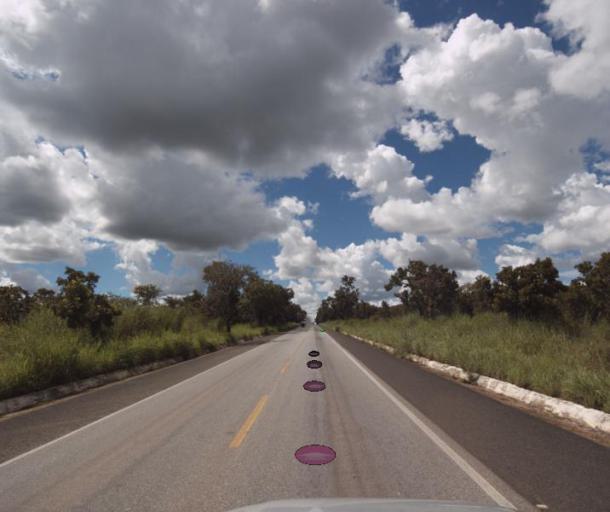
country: BR
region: Goias
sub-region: Porangatu
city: Porangatu
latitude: -13.7993
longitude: -49.0366
